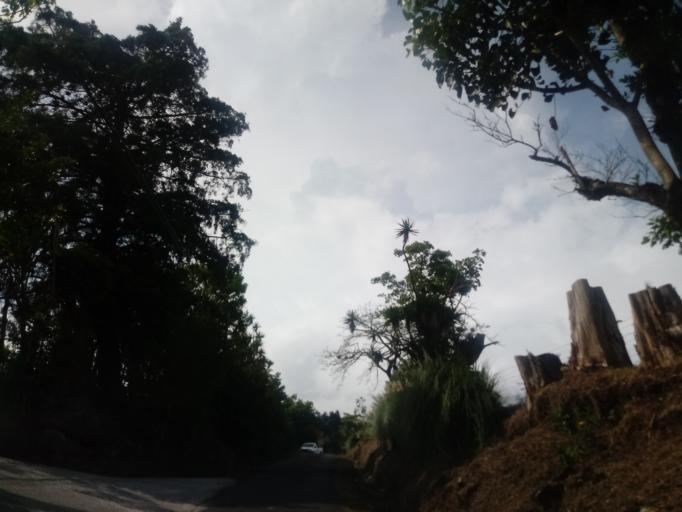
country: CR
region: Heredia
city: Angeles
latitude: 10.0359
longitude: -84.0410
